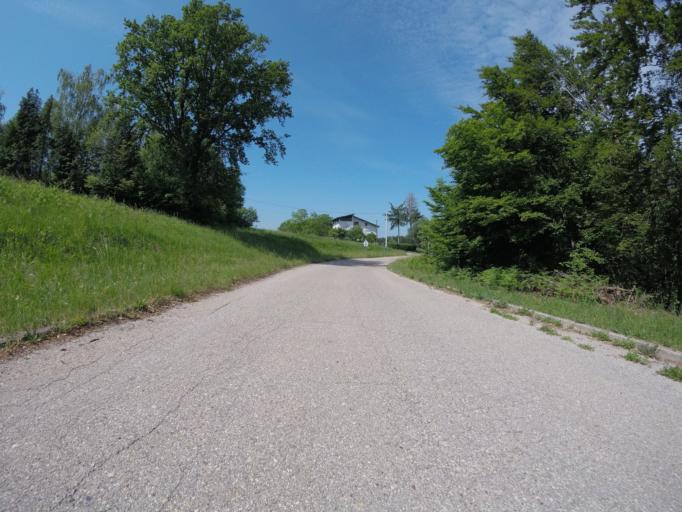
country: HR
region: Zagrebacka
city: Mraclin
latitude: 45.5760
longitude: 16.0085
